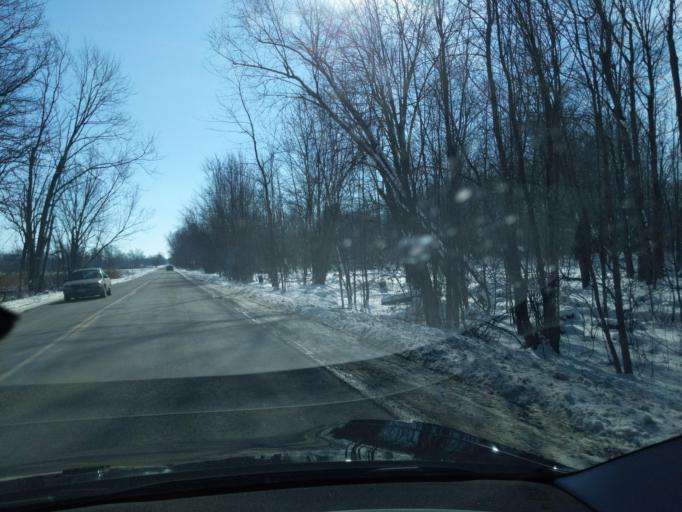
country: US
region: Michigan
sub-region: Livingston County
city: Fowlerville
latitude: 42.5987
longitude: -84.0751
